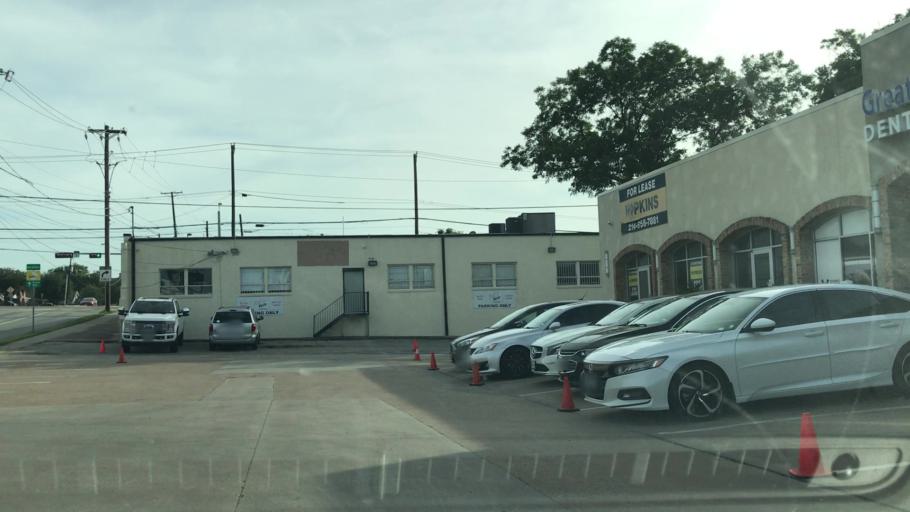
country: US
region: Texas
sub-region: Dallas County
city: Dallas
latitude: 32.8102
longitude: -96.8197
